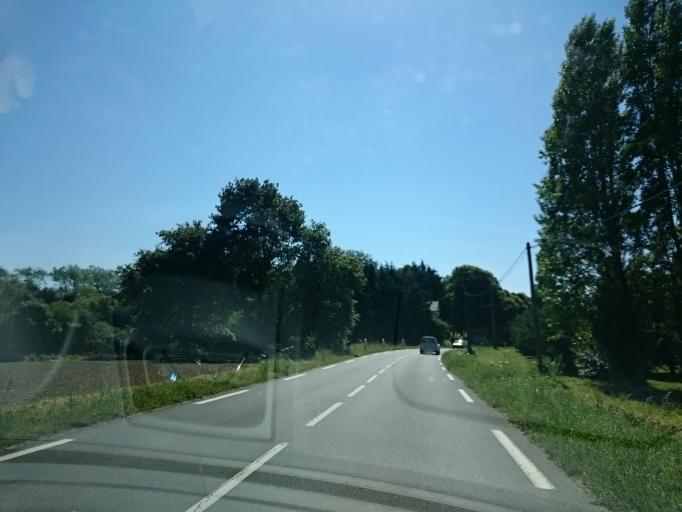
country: FR
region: Brittany
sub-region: Departement d'Ille-et-Vilaine
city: Saint-Coulomb
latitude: 48.6737
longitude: -1.9228
